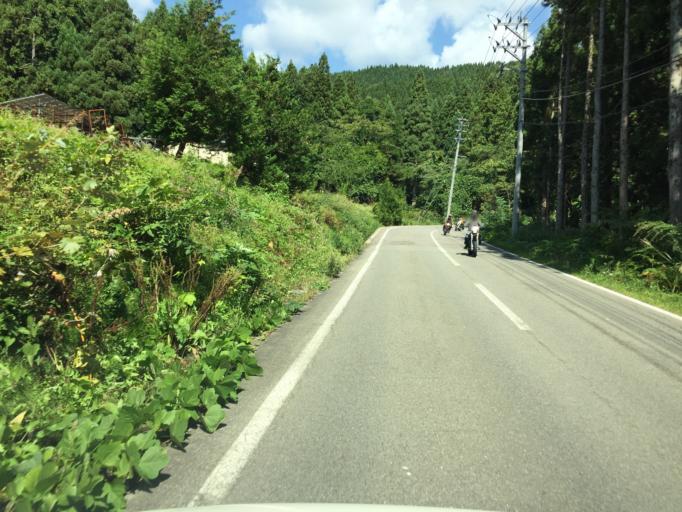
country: JP
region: Fukushima
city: Inawashiro
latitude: 37.5772
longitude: 140.0204
